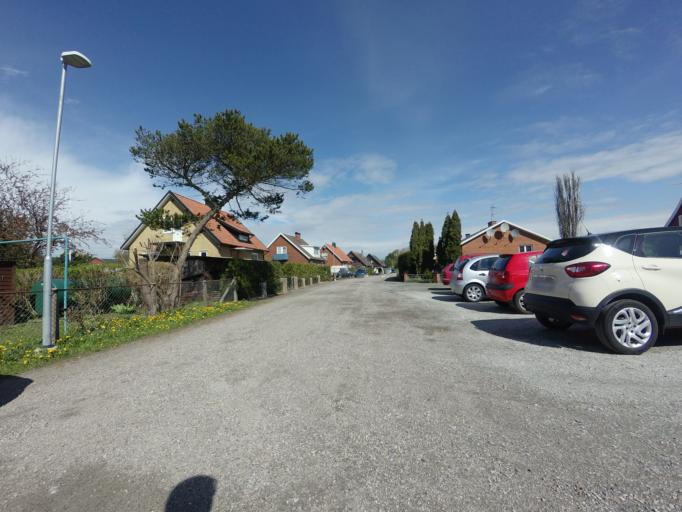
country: SE
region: Skane
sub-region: Malmo
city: Tygelsjo
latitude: 55.4943
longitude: 13.0016
